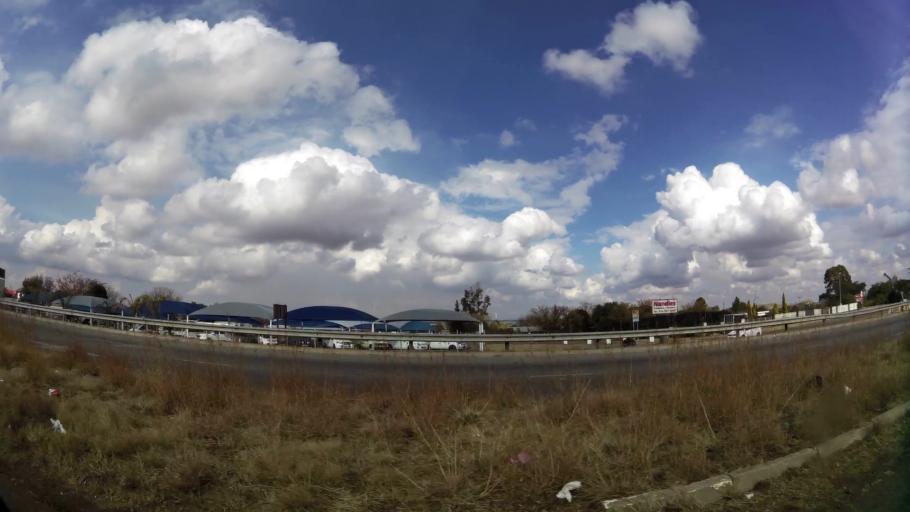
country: ZA
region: Gauteng
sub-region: Sedibeng District Municipality
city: Vanderbijlpark
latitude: -26.7387
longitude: 27.8206
